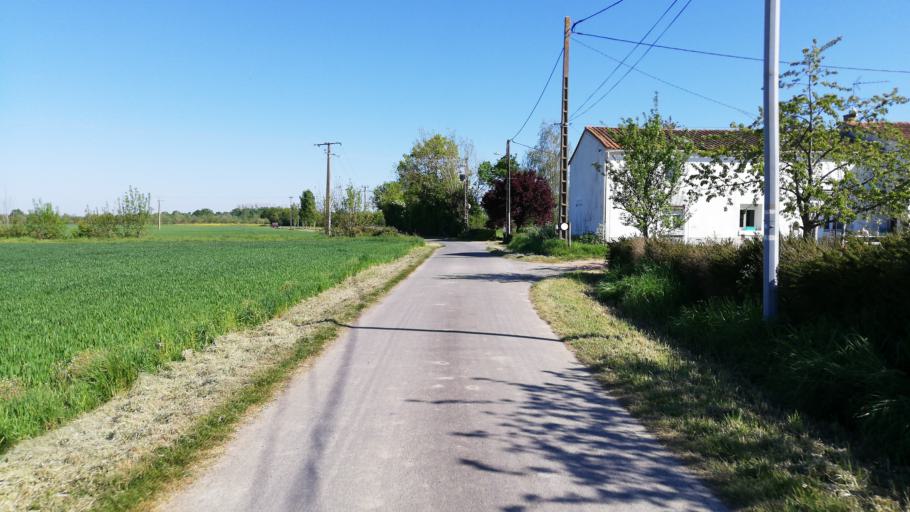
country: FR
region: Pays de la Loire
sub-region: Departement de la Vendee
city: Maillezais
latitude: 46.3290
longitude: -0.7503
